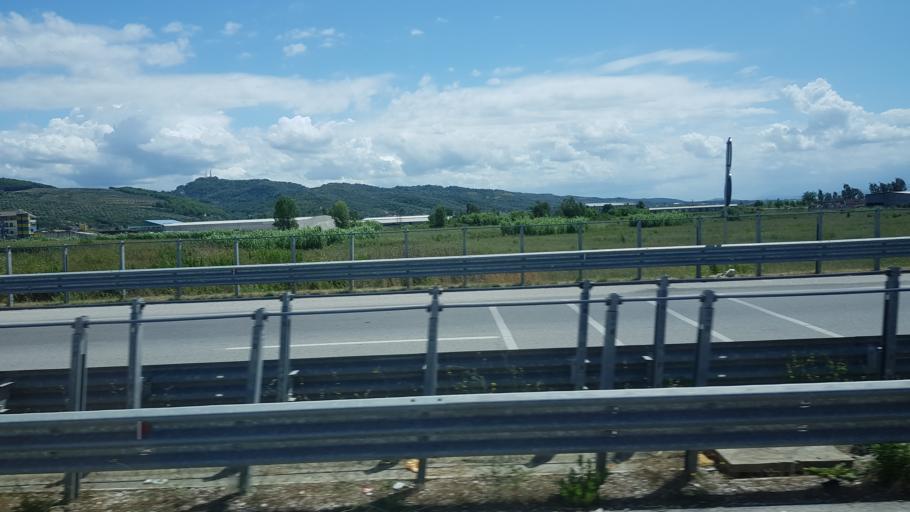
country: AL
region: Fier
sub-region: Rrethi i Fierit
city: Levan
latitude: 40.6671
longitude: 19.4775
